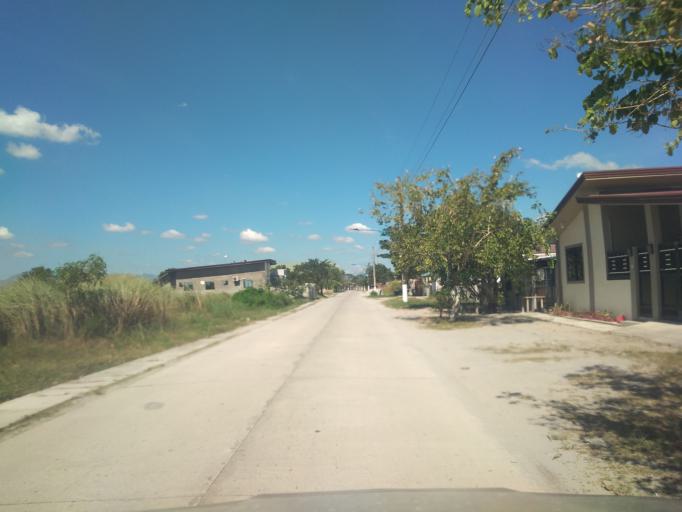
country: PH
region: Central Luzon
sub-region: Province of Pampanga
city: Balas
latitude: 15.0393
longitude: 120.6180
